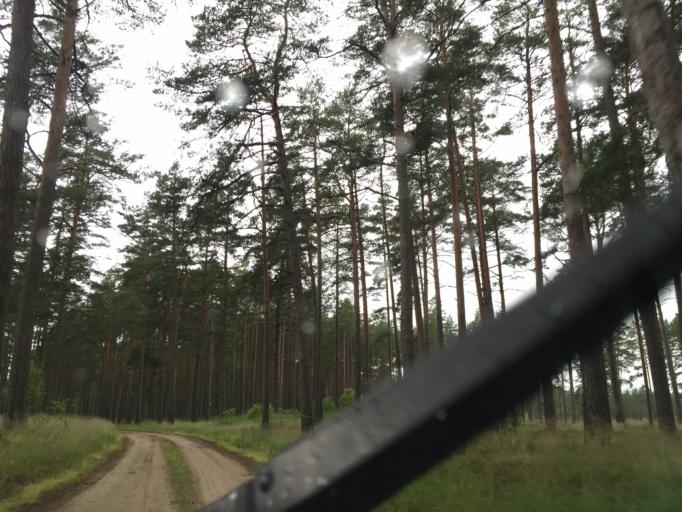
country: LV
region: Riga
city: Jaunciems
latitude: 57.0601
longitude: 24.1948
